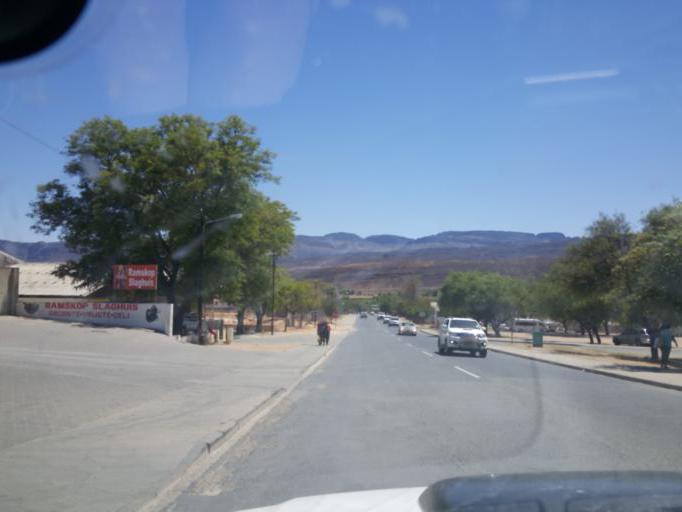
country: ZA
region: Western Cape
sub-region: West Coast District Municipality
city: Clanwilliam
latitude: -32.1864
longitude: 18.8907
